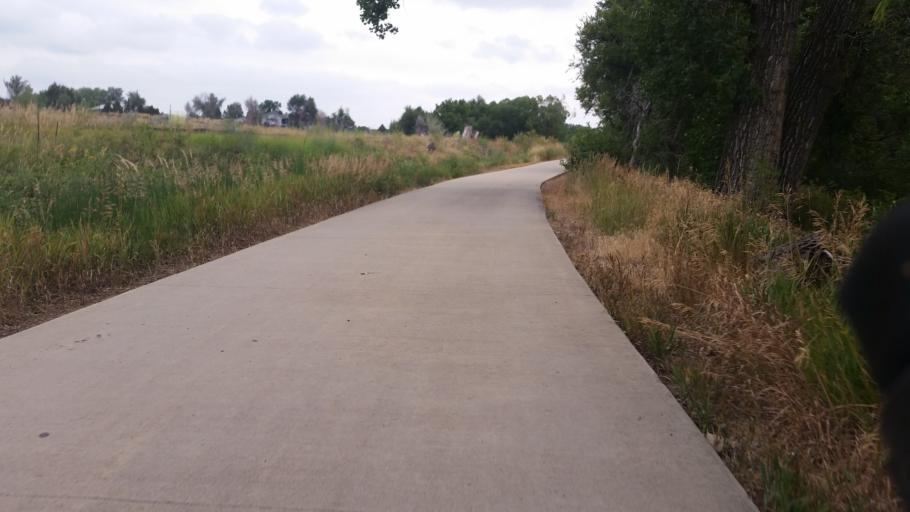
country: US
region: Colorado
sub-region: Adams County
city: Twin Lakes
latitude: 39.8180
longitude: -104.9991
